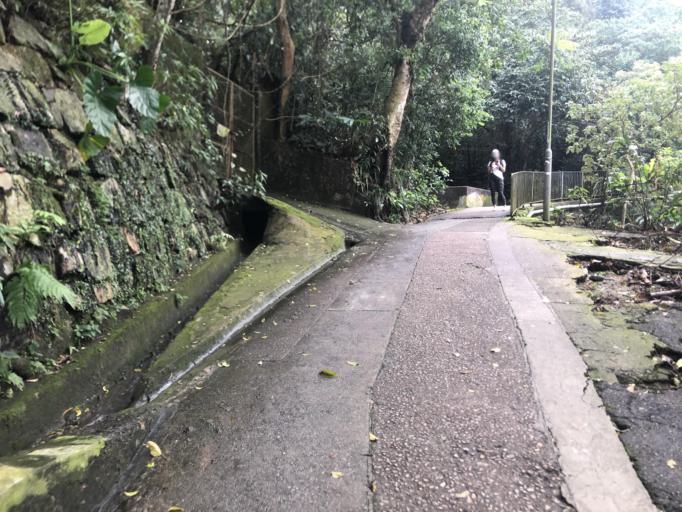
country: HK
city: Hong Kong
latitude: 22.2786
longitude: 114.1385
